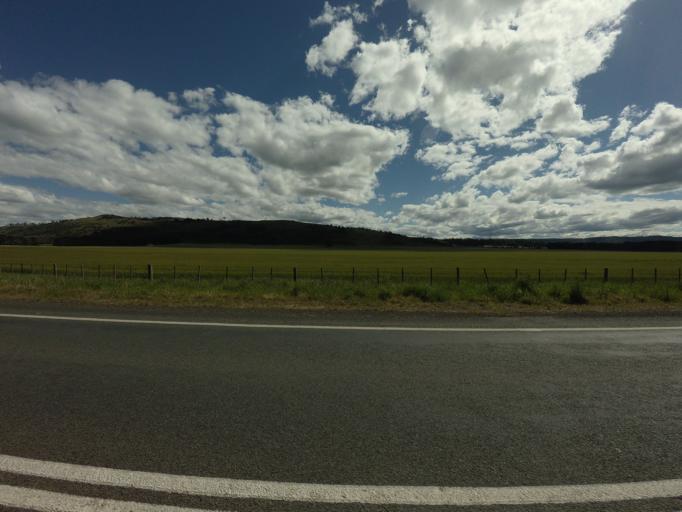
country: AU
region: Tasmania
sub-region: Northern Midlands
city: Evandale
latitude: -42.0364
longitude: 147.4824
